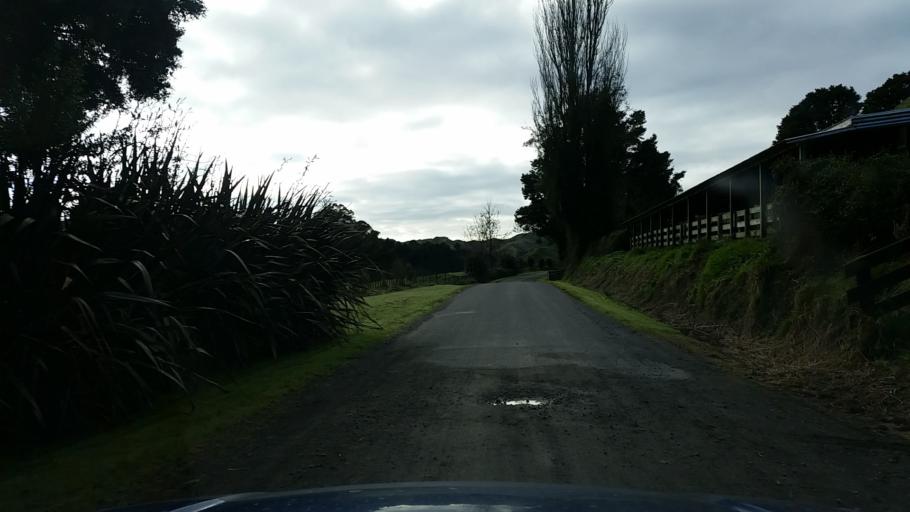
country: NZ
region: Taranaki
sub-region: New Plymouth District
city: Waitara
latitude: -39.0765
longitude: 174.8109
